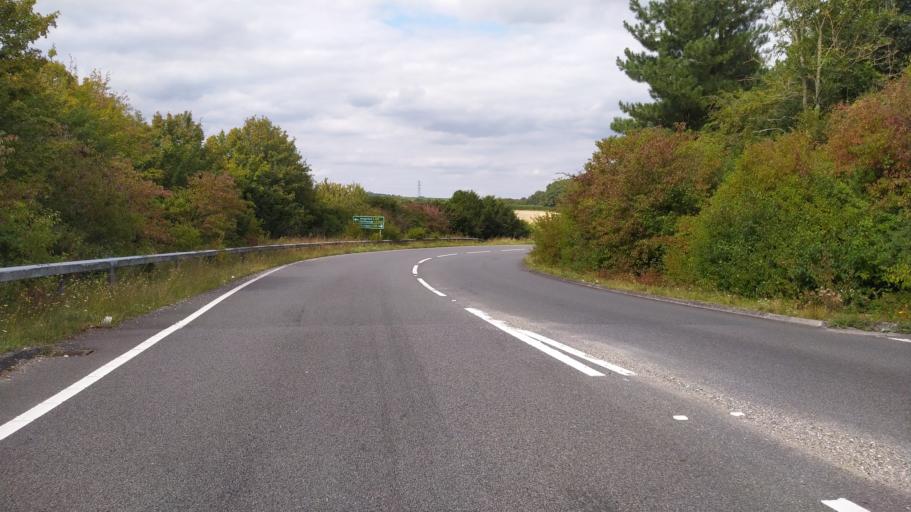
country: GB
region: England
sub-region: Wiltshire
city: Tidworth
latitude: 51.1926
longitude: -1.6717
